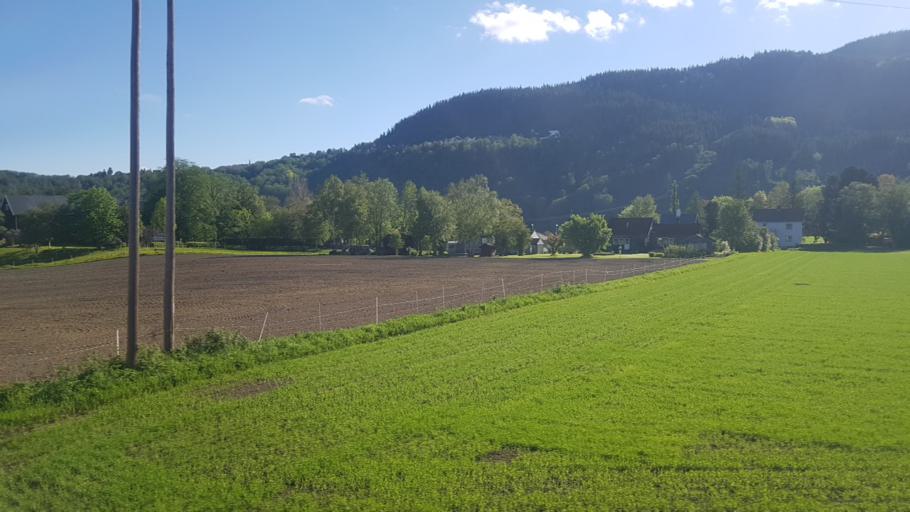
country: NO
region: Sor-Trondelag
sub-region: Melhus
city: Melhus
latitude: 63.2806
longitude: 10.2657
